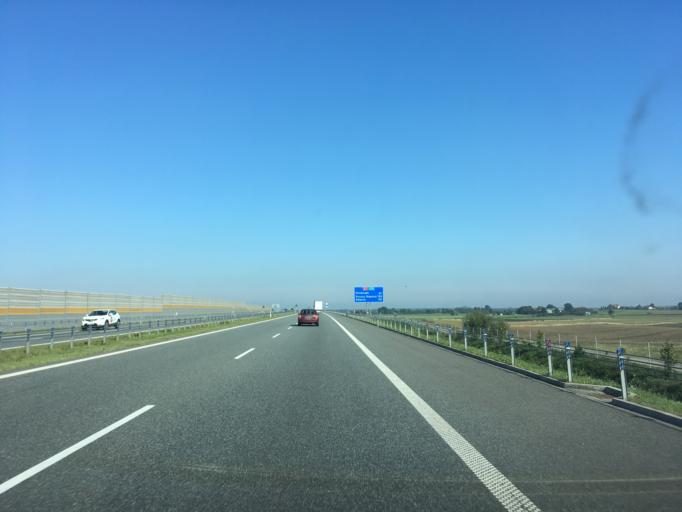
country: PL
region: Kujawsko-Pomorskie
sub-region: Powiat torunski
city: Lubicz Dolny
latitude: 53.1005
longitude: 18.7491
